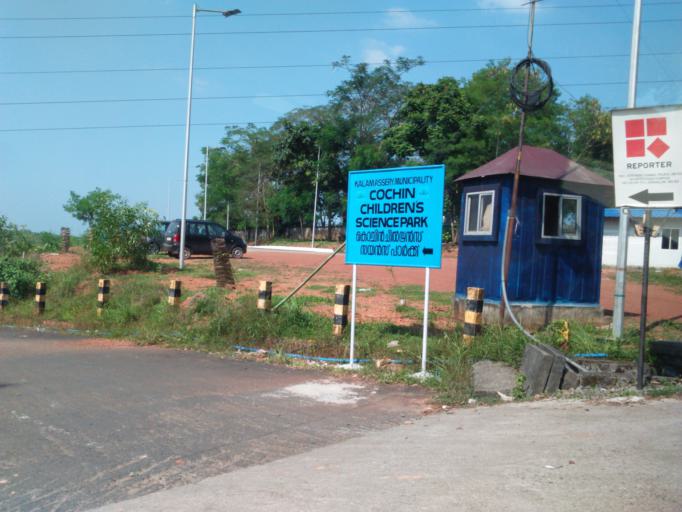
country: IN
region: Kerala
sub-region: Ernakulam
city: Aluva
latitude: 10.0557
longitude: 76.3559
